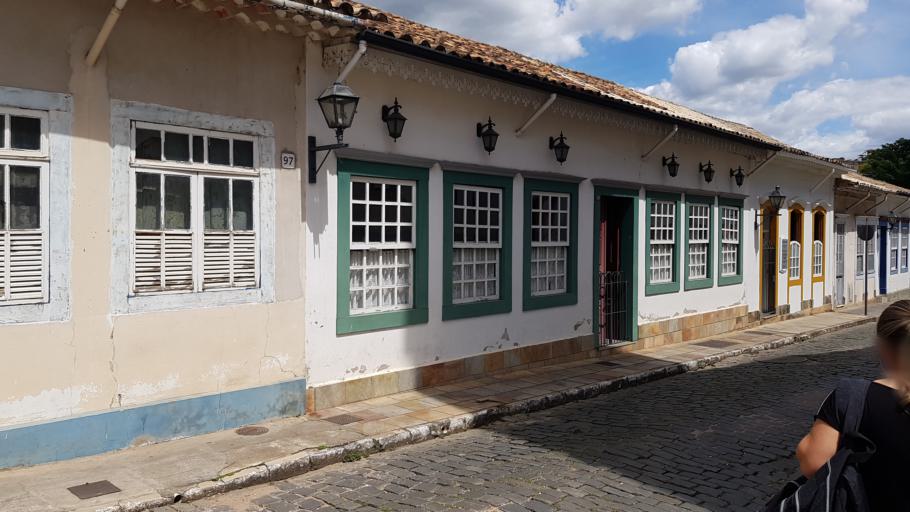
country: BR
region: Minas Gerais
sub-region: Sao Joao Del Rei
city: Sao Joao del Rei
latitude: -21.1364
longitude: -44.2626
